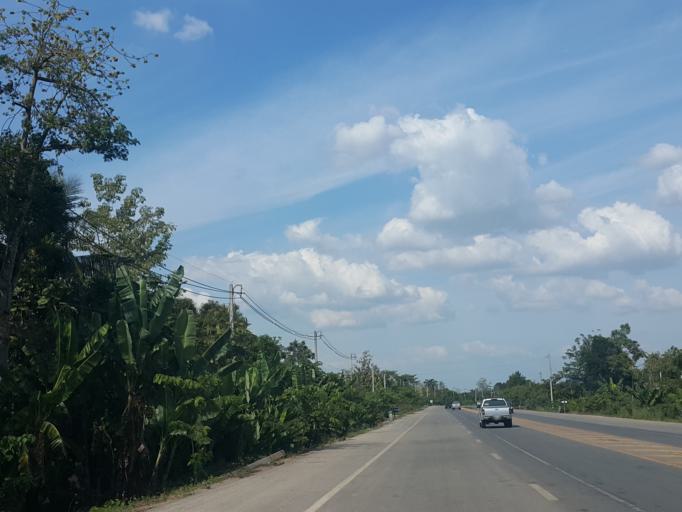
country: TH
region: Sukhothai
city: Si Samrong
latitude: 17.2336
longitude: 99.8463
